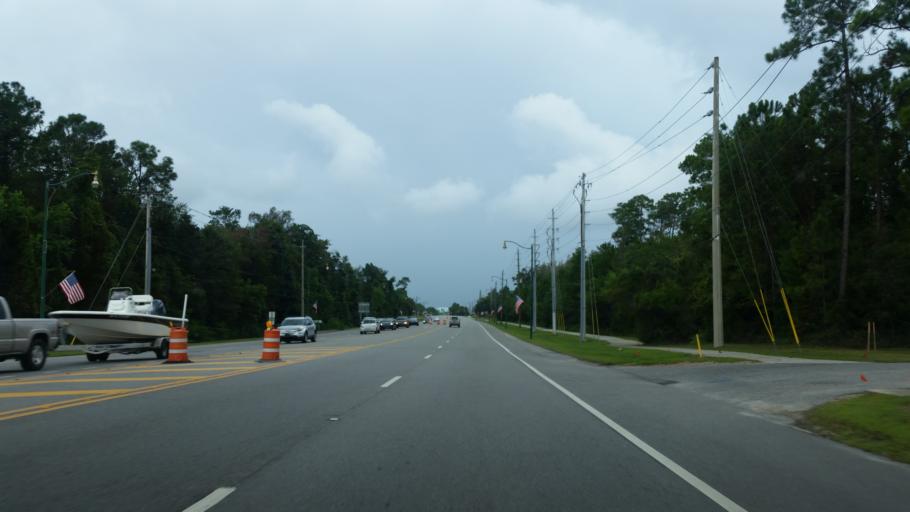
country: US
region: Alabama
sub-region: Baldwin County
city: Orange Beach
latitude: 30.2906
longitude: -87.5814
